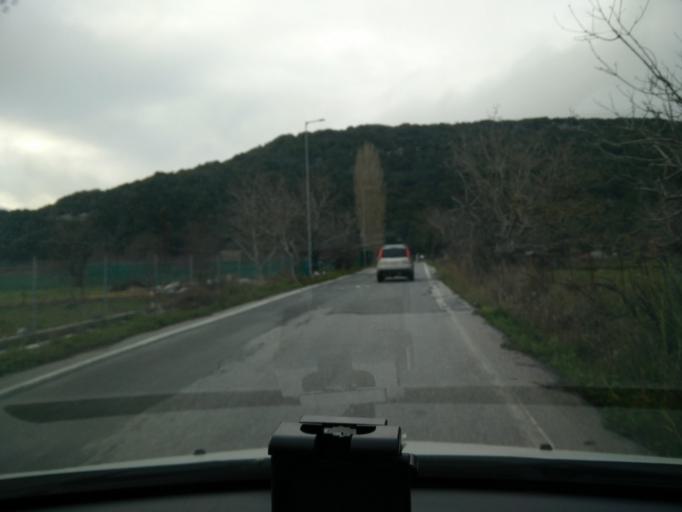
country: GR
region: Crete
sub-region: Nomos Irakleiou
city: Mokhos
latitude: 35.2036
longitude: 25.4764
